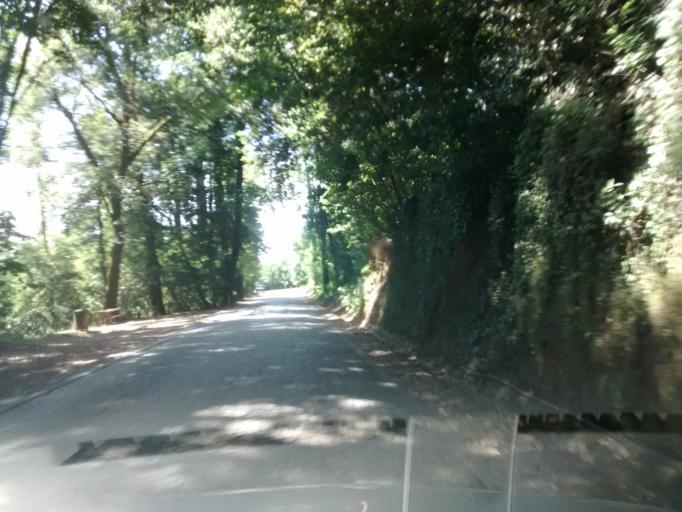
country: PT
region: Aveiro
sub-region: Mealhada
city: Pampilhosa do Botao
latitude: 40.3793
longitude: -8.3707
